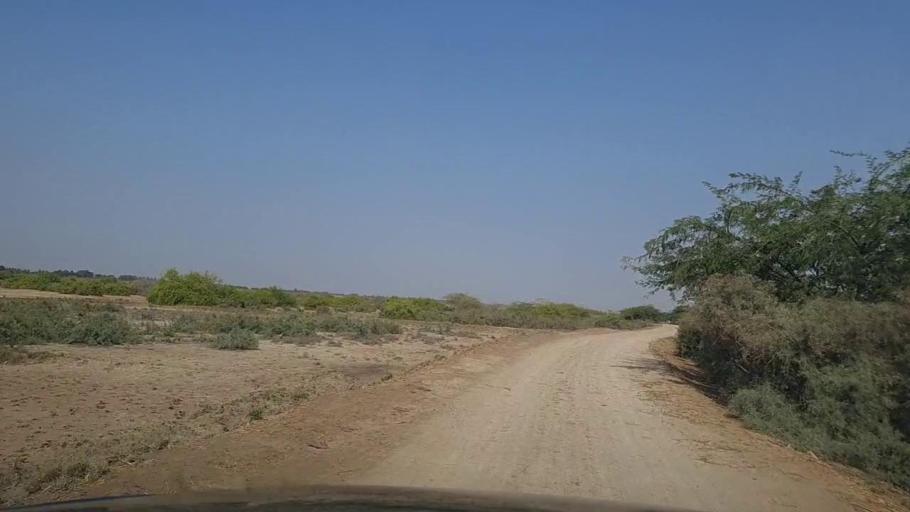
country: PK
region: Sindh
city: Thatta
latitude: 24.6475
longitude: 67.8170
